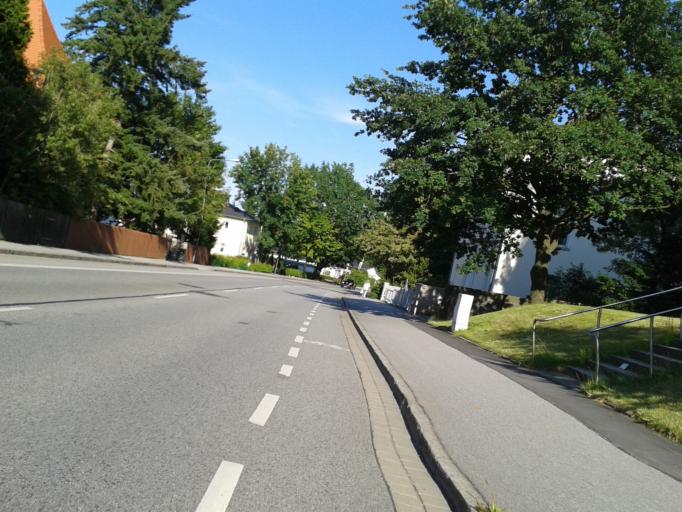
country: DE
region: Saxony
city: Albertstadt
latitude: 51.1189
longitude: 13.7710
